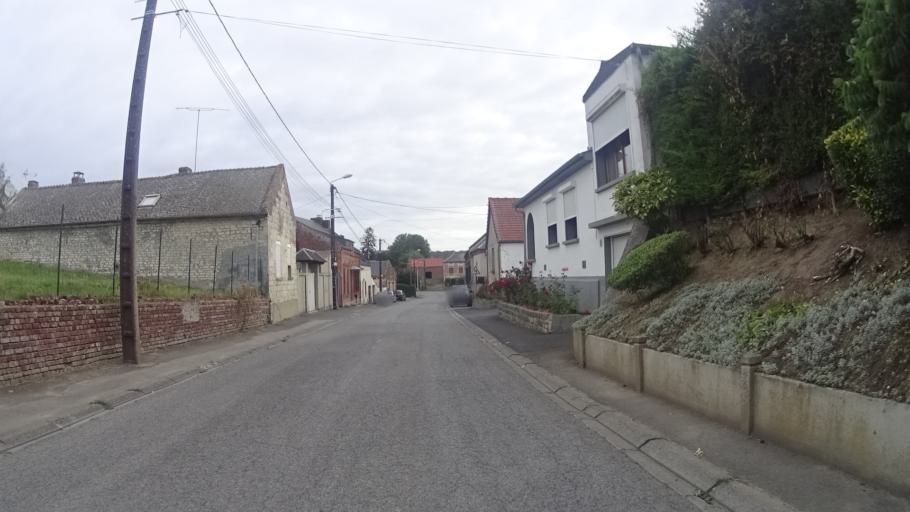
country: FR
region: Picardie
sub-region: Departement de l'Aisne
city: Origny-Sainte-Benoite
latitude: 49.8849
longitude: 3.5528
